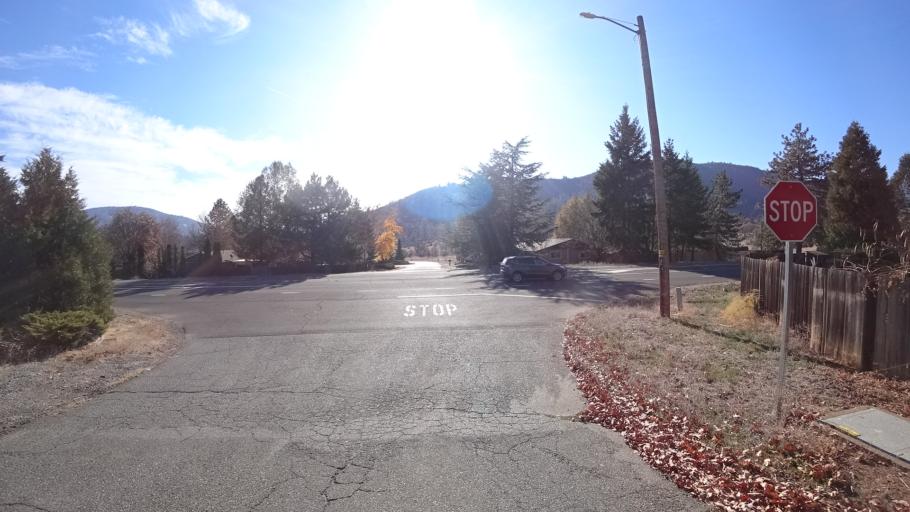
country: US
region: California
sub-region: Siskiyou County
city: Yreka
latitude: 41.6924
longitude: -122.6541
